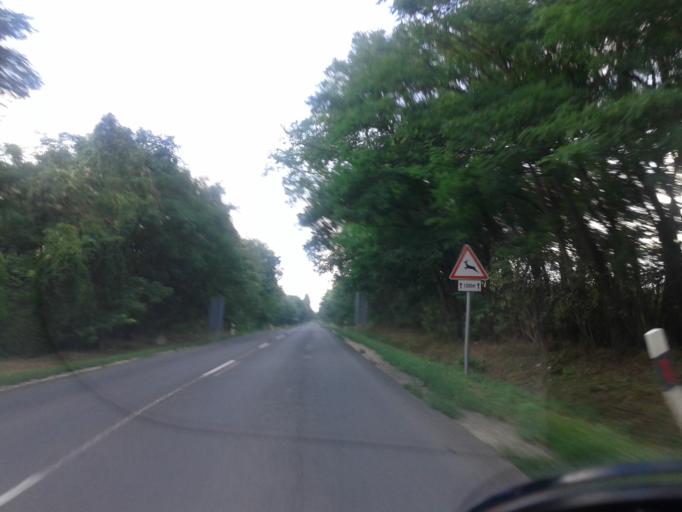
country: HU
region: Pest
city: Kiskunlachaza
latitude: 47.2354
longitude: 19.0209
